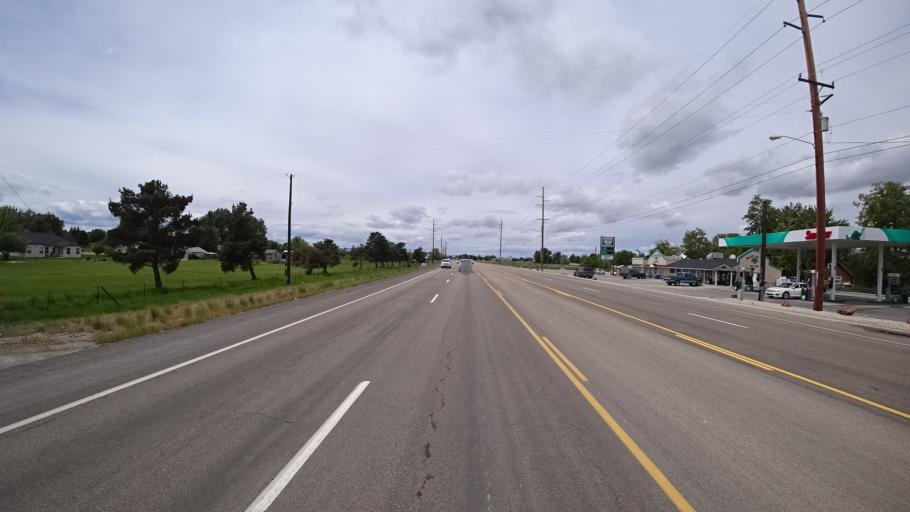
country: US
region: Idaho
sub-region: Ada County
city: Eagle
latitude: 43.6949
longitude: -116.4062
